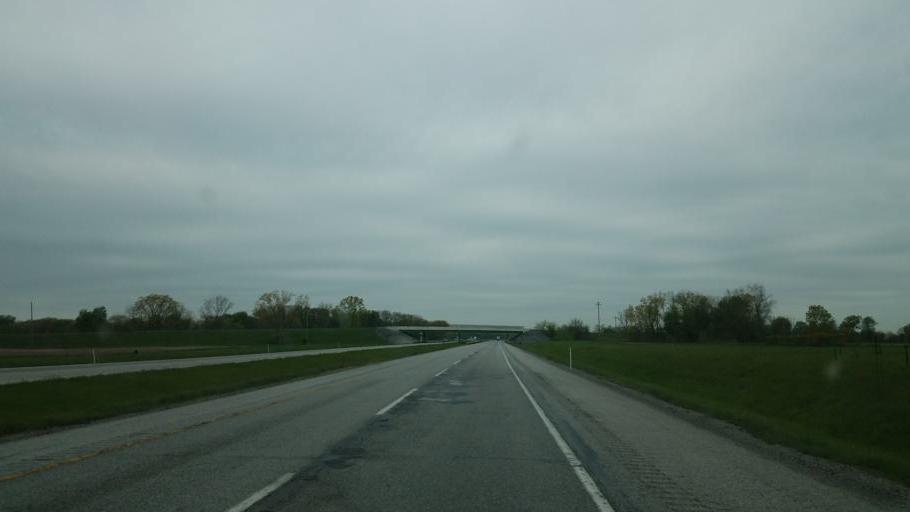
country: US
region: Michigan
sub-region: Saint Joseph County
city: White Pigeon
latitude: 41.7500
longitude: -85.5603
